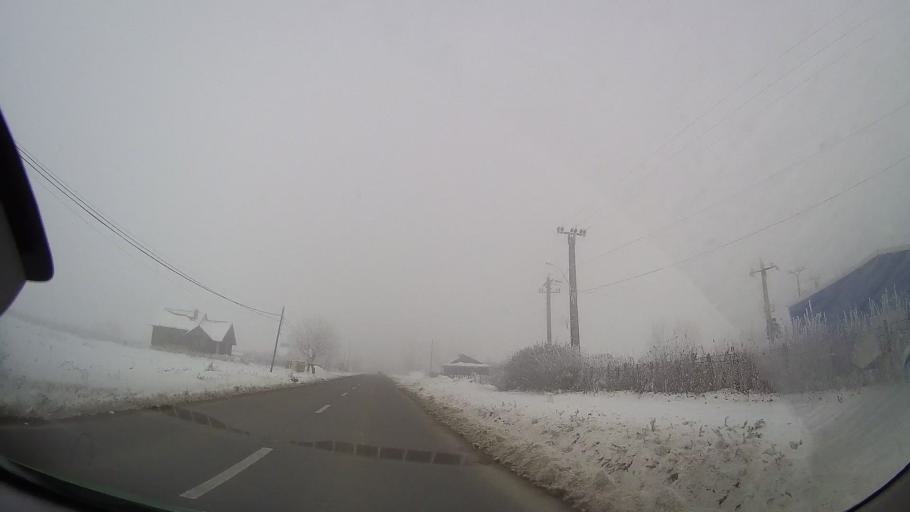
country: RO
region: Iasi
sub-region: Comuna Stolniceni-Prajescu
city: Stolniceni-Prajescu
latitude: 47.1983
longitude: 26.7391
